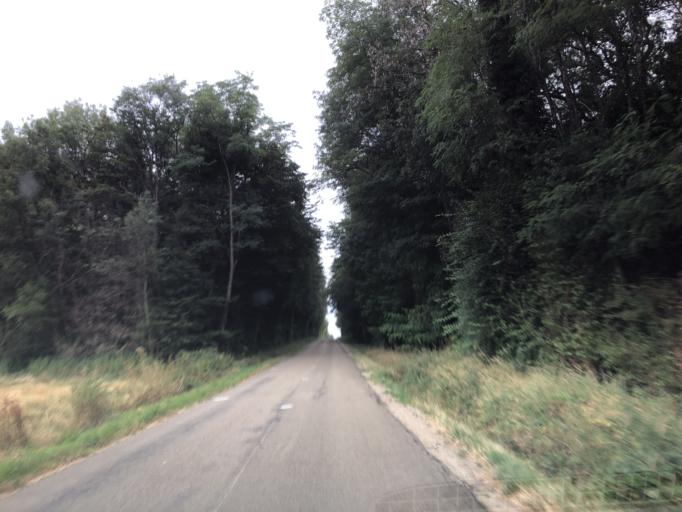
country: FR
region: Centre
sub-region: Departement du Loiret
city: Courtenay
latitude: 47.9943
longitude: 3.1433
